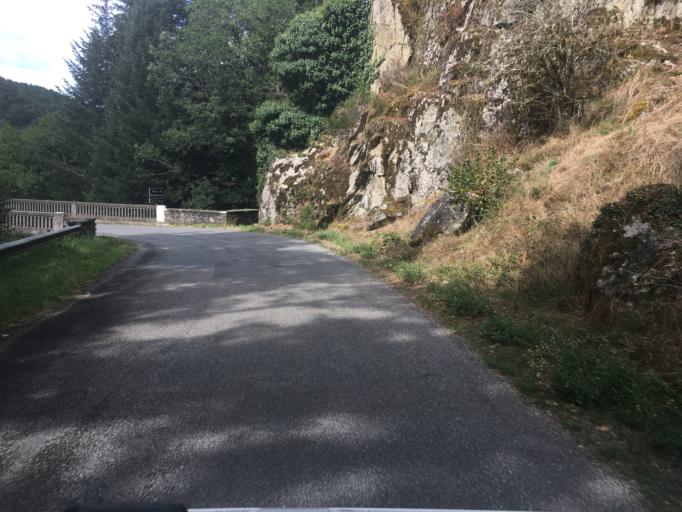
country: FR
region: Auvergne
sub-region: Departement du Cantal
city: Champagnac
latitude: 45.4370
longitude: 2.3962
